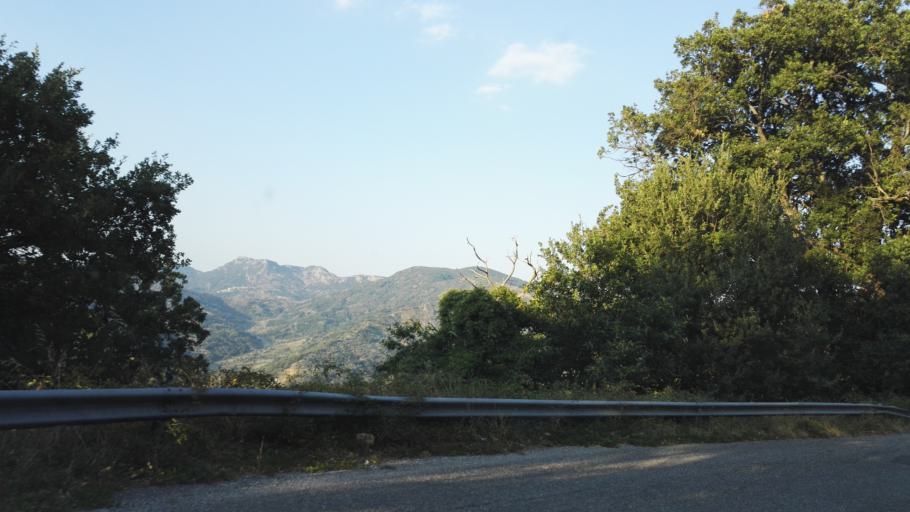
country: IT
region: Calabria
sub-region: Provincia di Reggio Calabria
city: Caulonia
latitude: 38.4060
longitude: 16.3657
